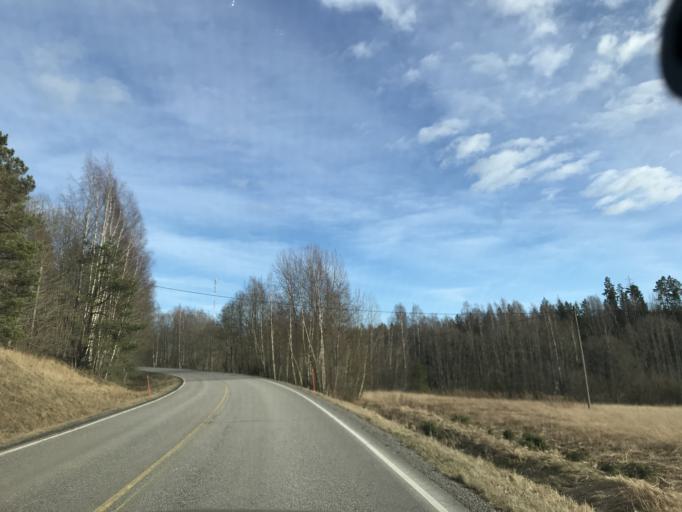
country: FI
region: Uusimaa
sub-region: Raaseporin
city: Ekenaes
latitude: 60.0839
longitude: 23.3900
